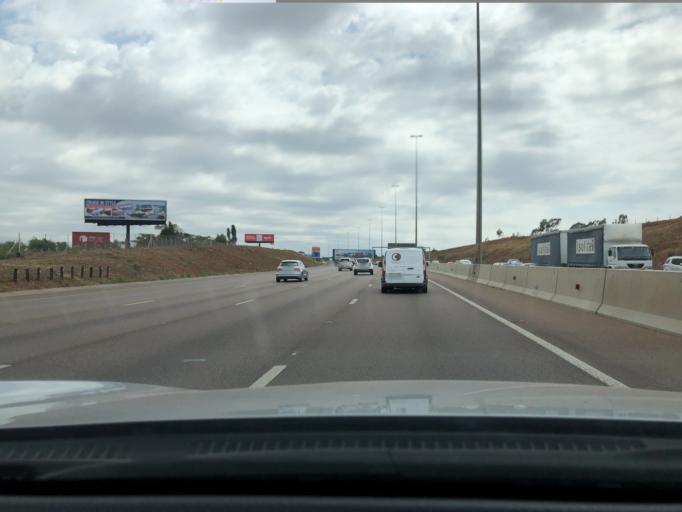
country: ZA
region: Gauteng
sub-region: City of Tshwane Metropolitan Municipality
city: Centurion
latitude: -25.8552
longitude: 28.2250
